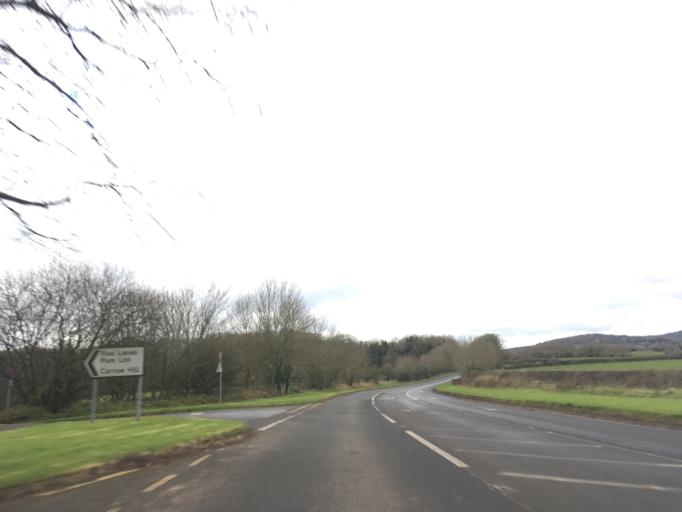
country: GB
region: Wales
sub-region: Newport
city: Llanvaches
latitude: 51.6136
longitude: -2.7980
